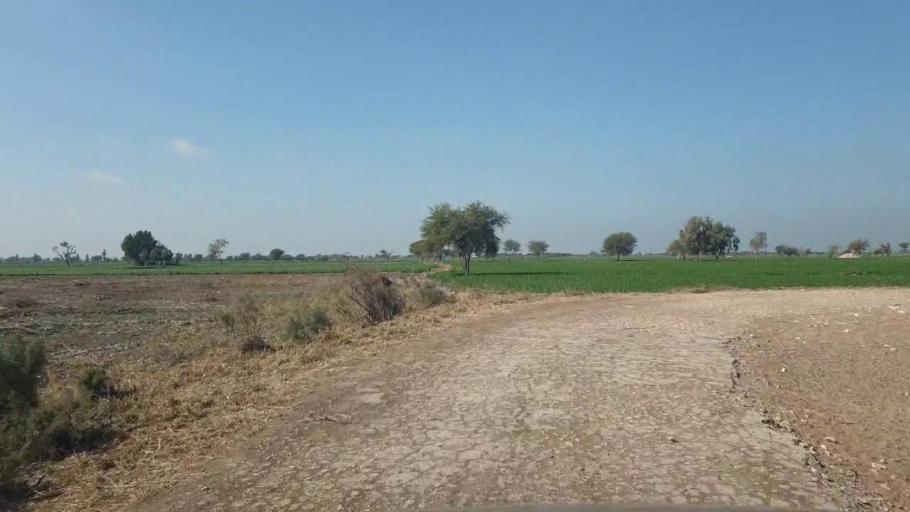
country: PK
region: Sindh
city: Bhit Shah
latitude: 25.8812
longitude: 68.5264
